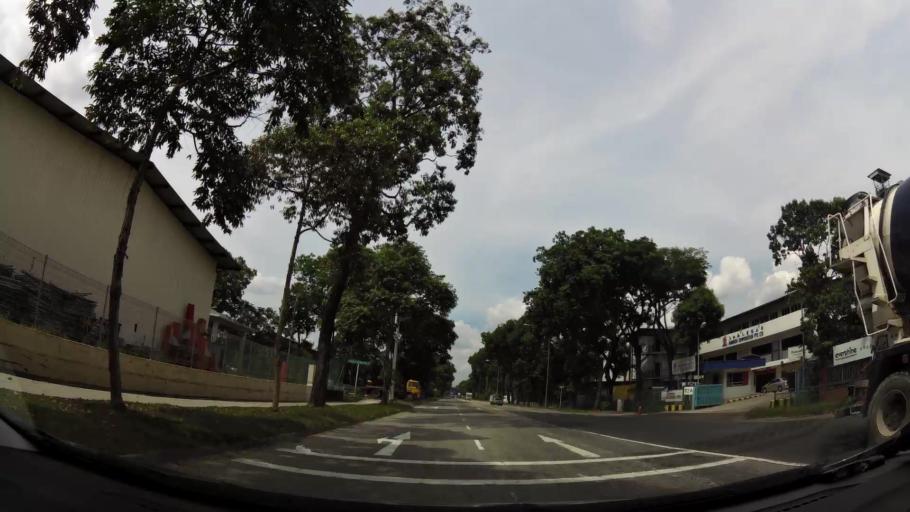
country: MY
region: Johor
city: Johor Bahru
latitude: 1.4170
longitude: 103.7512
